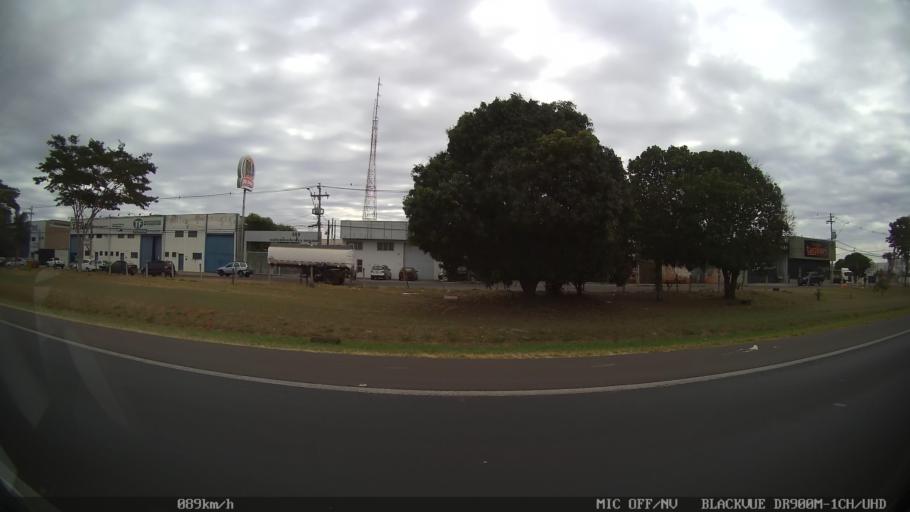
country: BR
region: Sao Paulo
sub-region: Sao Jose Do Rio Preto
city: Sao Jose do Rio Preto
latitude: -20.8105
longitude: -49.4927
